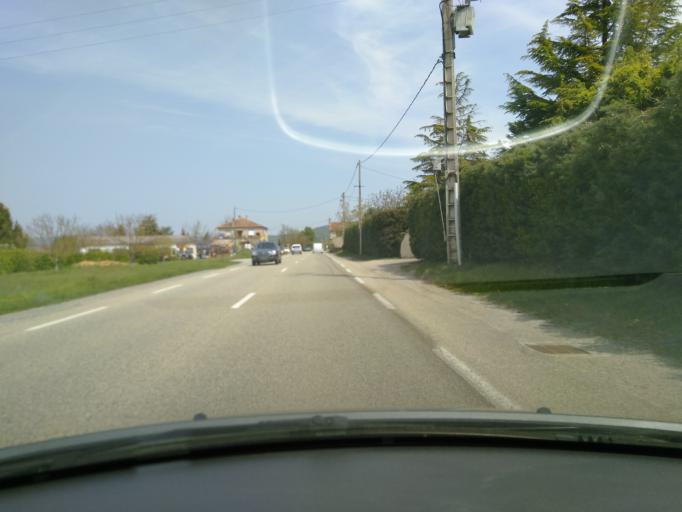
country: FR
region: Rhone-Alpes
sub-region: Departement de l'Ardeche
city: Saint-Sernin
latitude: 44.5255
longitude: 4.4089
